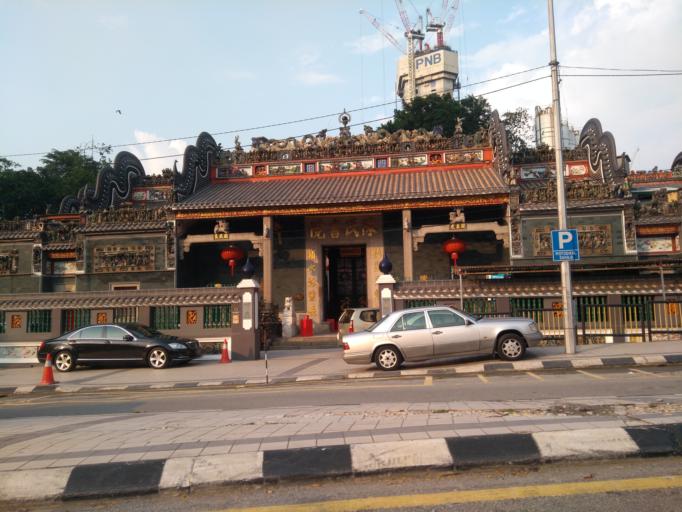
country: MY
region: Kuala Lumpur
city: Kuala Lumpur
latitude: 3.1402
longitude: 101.6982
